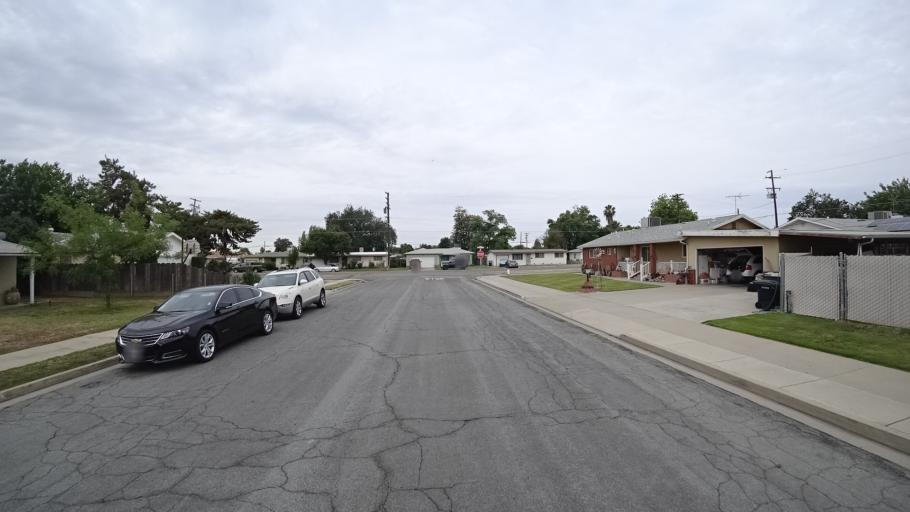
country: US
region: California
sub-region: Kings County
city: Hanford
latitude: 36.3380
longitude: -119.6572
